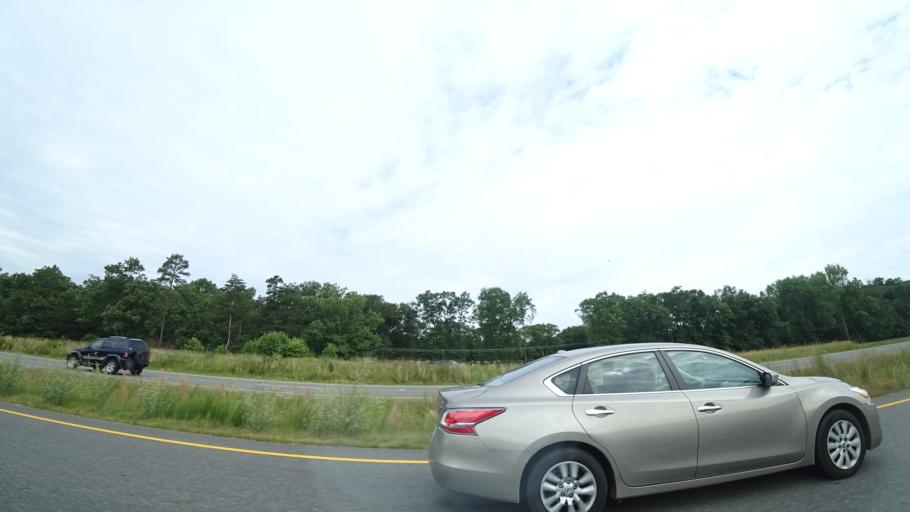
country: US
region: Virginia
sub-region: Spotsylvania County
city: Spotsylvania
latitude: 38.1925
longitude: -77.6182
